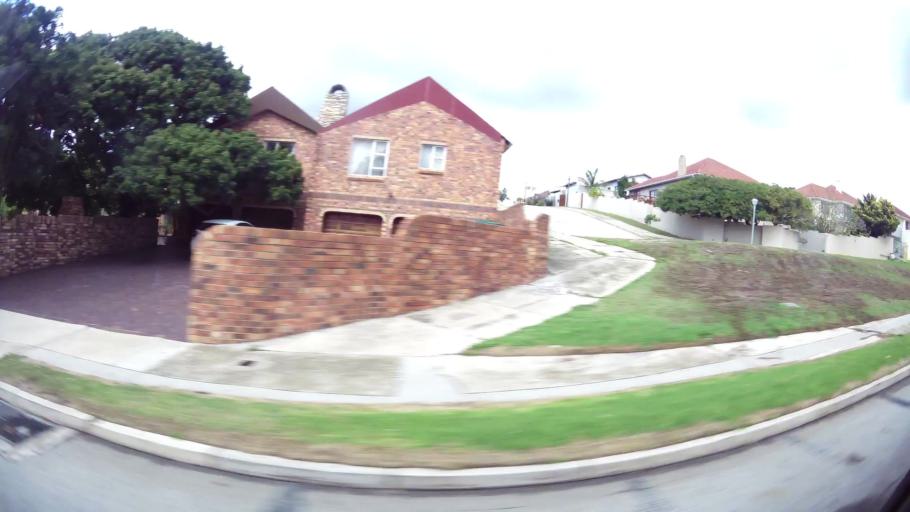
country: ZA
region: Eastern Cape
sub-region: Nelson Mandela Bay Metropolitan Municipality
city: Port Elizabeth
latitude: -33.9513
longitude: 25.5980
